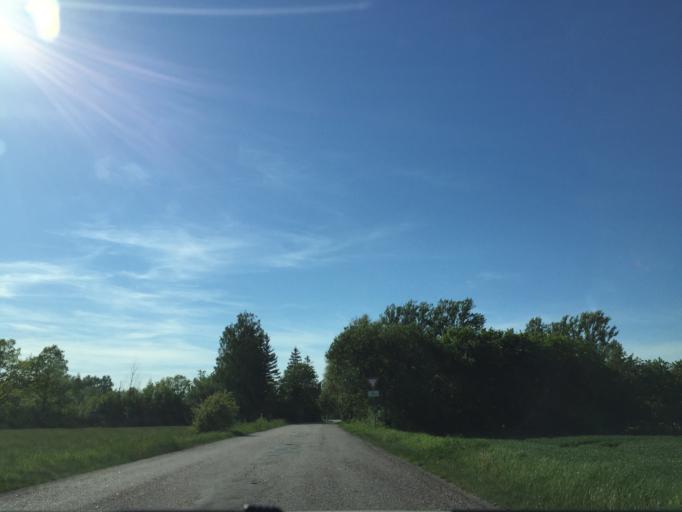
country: LV
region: Jelgava
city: Jelgava
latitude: 56.5287
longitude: 23.7092
